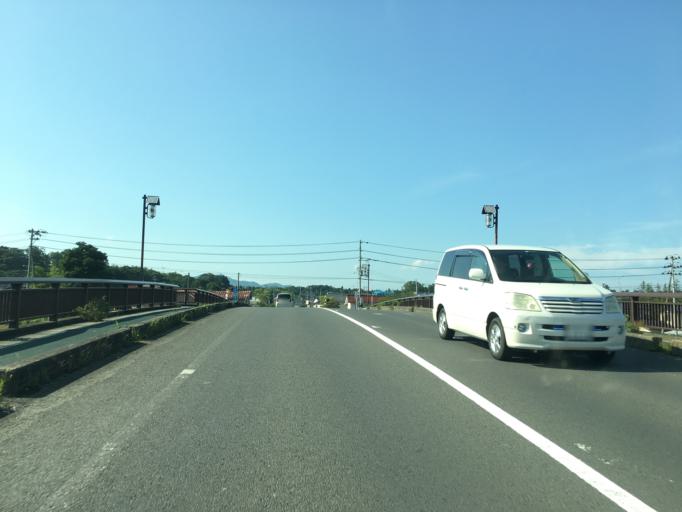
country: JP
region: Miyagi
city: Marumori
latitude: 37.7899
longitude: 140.9128
